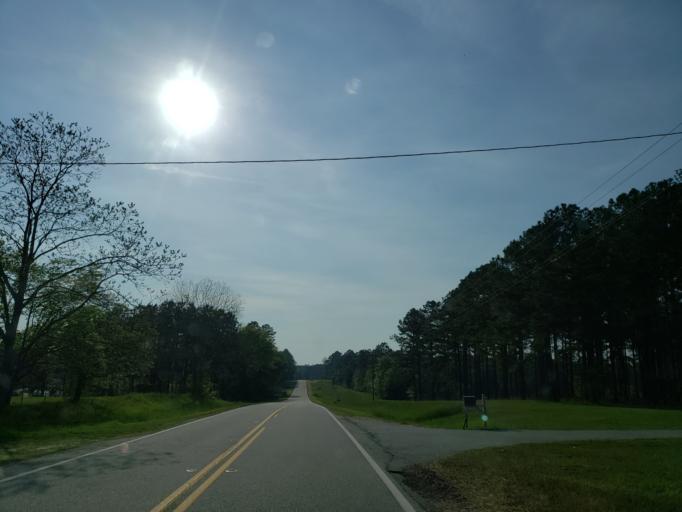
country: US
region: Georgia
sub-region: Tift County
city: Tifton
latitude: 31.5586
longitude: -83.4962
